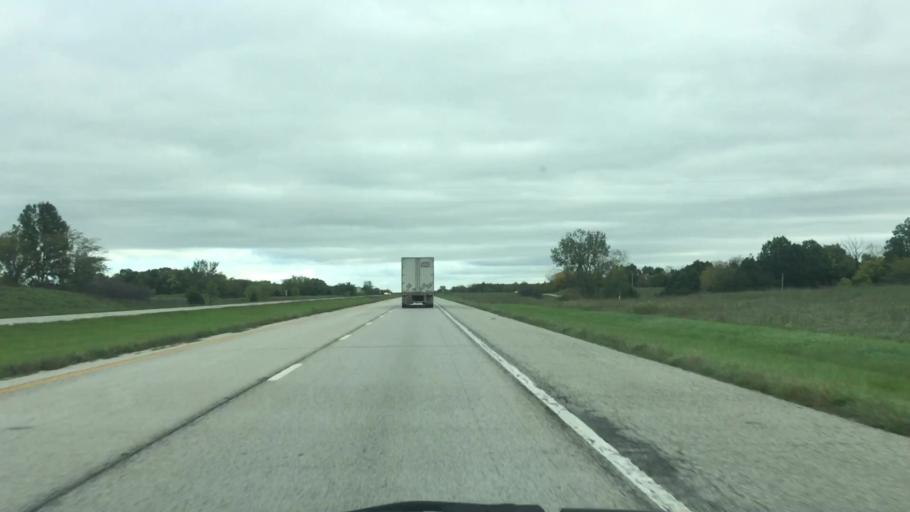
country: US
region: Missouri
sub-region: Harrison County
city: Bethany
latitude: 40.1258
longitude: -94.0544
